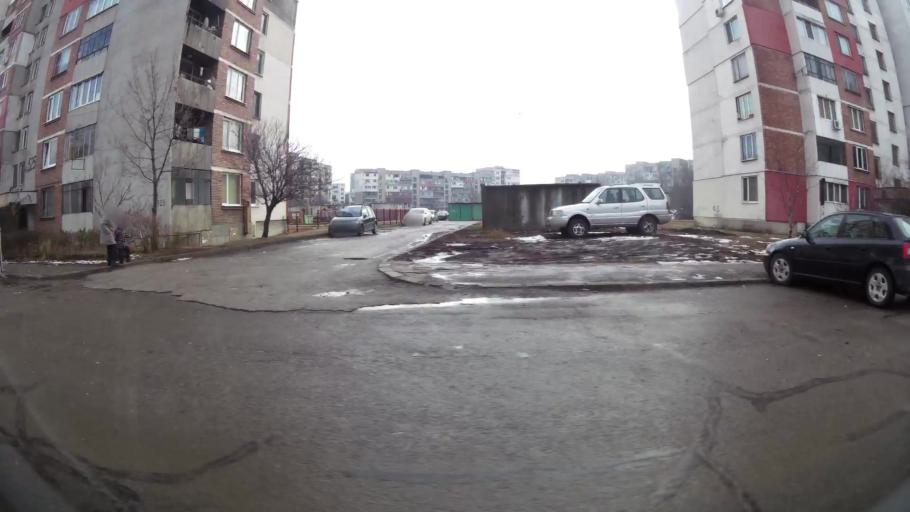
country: BG
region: Sofiya
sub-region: Obshtina Bozhurishte
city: Bozhurishte
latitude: 42.7177
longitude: 23.2381
